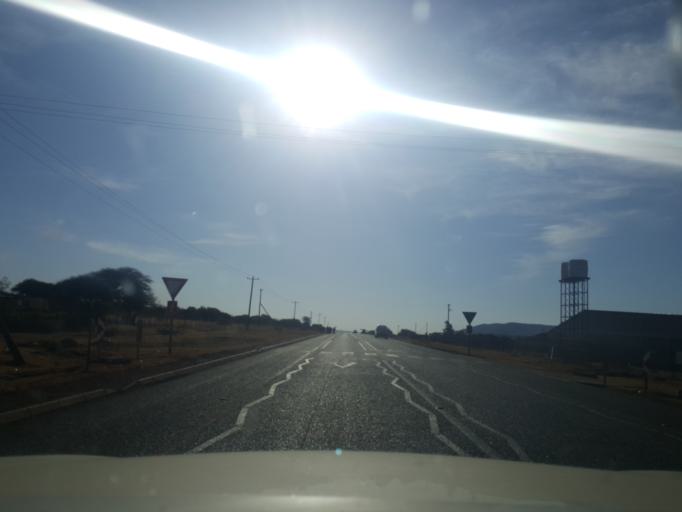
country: ZA
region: North-West
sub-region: Ngaka Modiri Molema District Municipality
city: Zeerust
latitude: -25.4677
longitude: 25.8918
